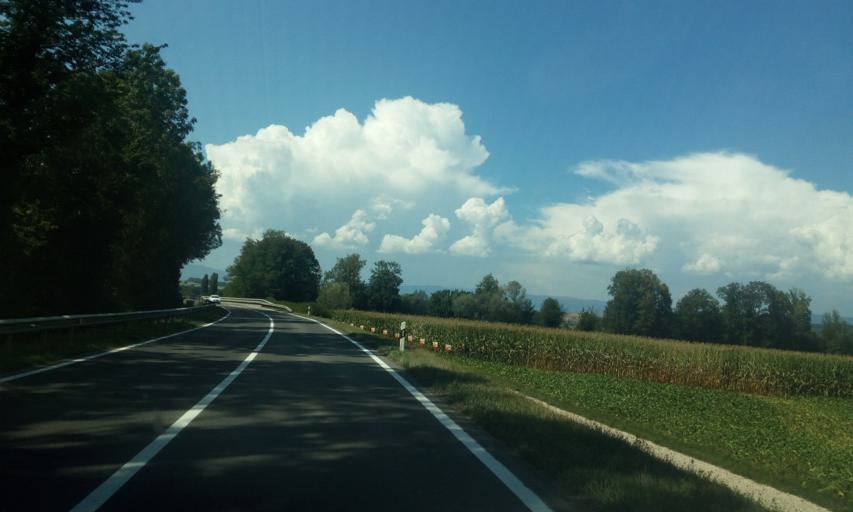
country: CH
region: Fribourg
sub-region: Broye District
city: Domdidier
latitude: 46.8883
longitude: 7.0182
